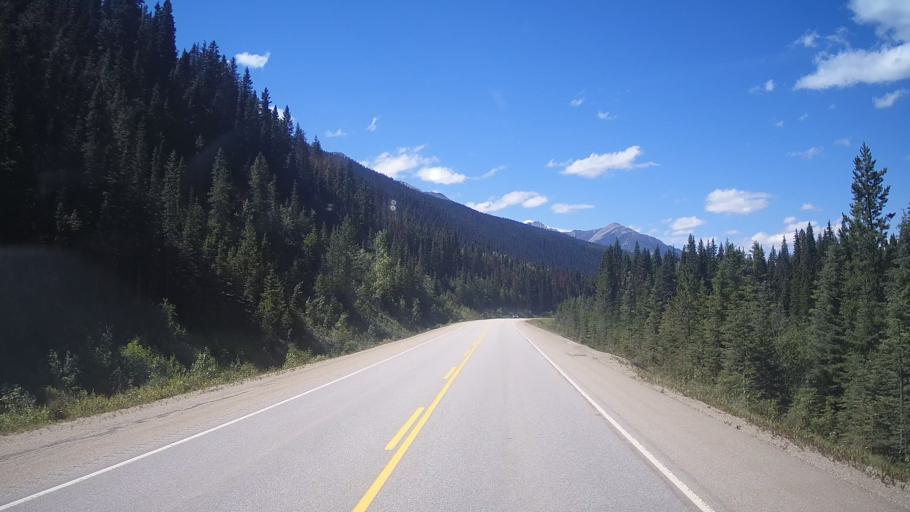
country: CA
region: Alberta
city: Jasper Park Lodge
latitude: 52.8633
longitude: -118.6576
